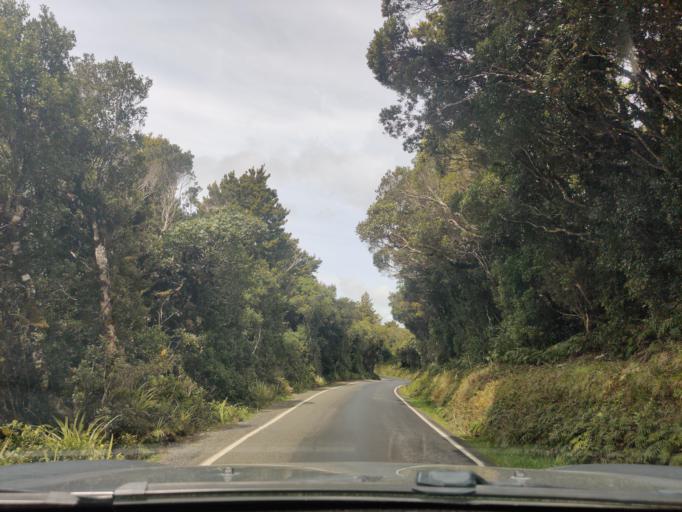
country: NZ
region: Taranaki
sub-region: South Taranaki District
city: Eltham
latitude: -39.3235
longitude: 174.1050
